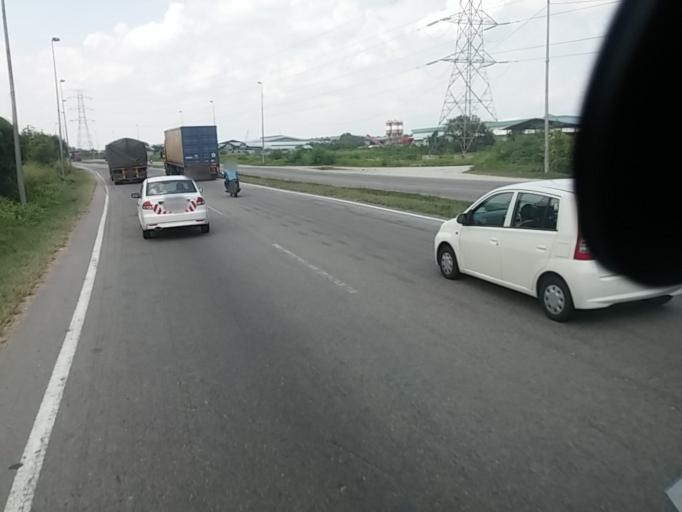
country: MY
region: Selangor
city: Klang
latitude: 2.9776
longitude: 101.3959
